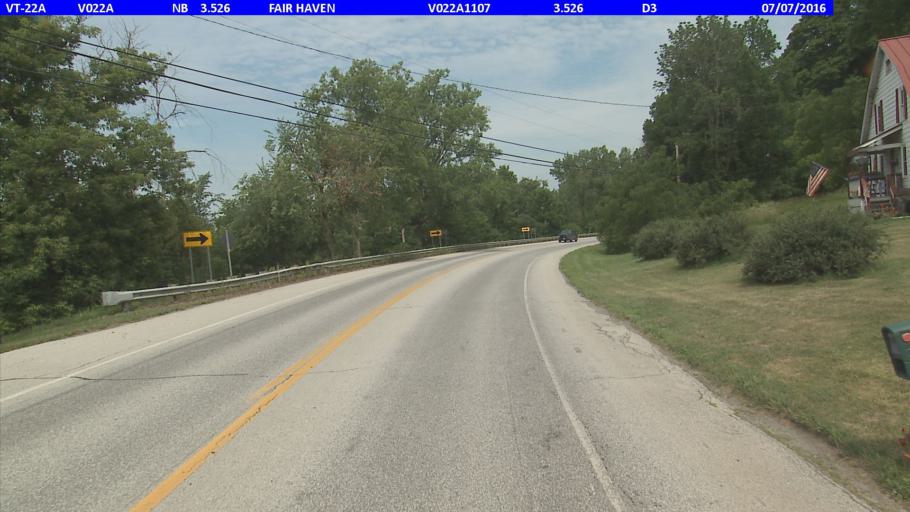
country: US
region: Vermont
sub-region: Rutland County
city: Fair Haven
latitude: 43.6158
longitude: -73.2936
